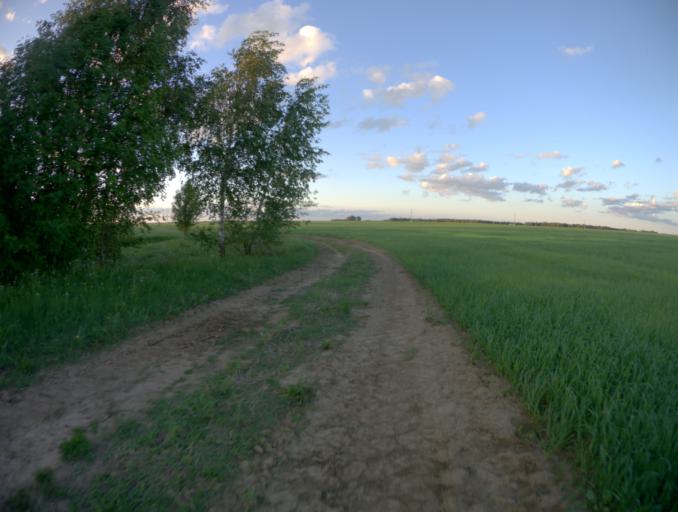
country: RU
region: Ivanovo
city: Gavrilov Posad
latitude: 56.5408
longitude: 40.1994
